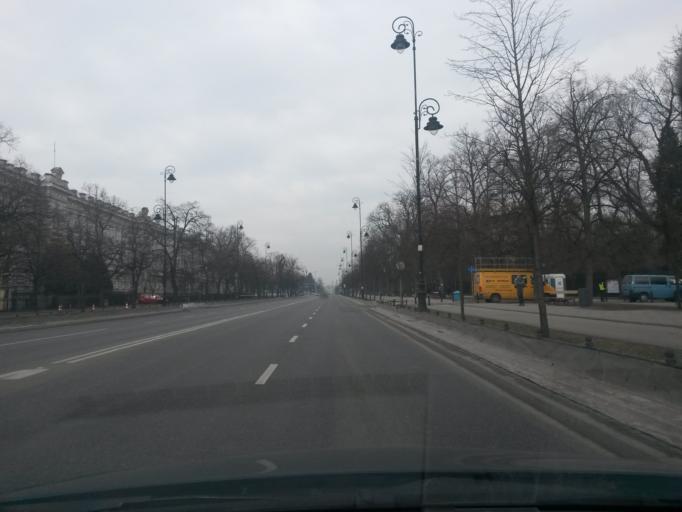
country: PL
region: Masovian Voivodeship
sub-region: Warszawa
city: Srodmiescie
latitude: 52.2165
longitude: 21.0260
